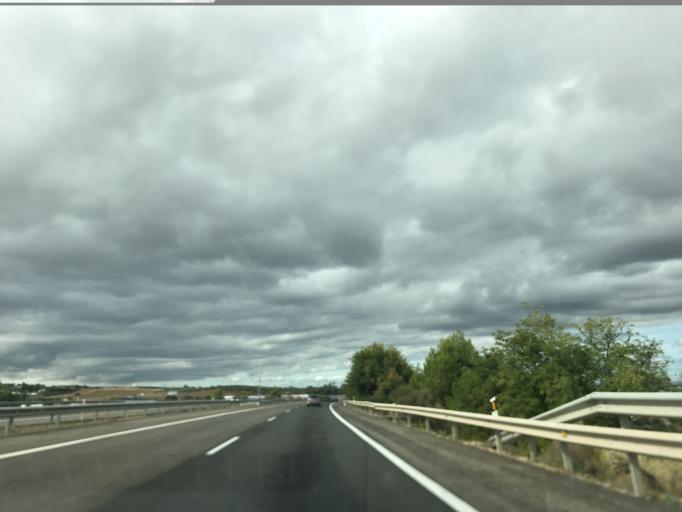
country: ES
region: Andalusia
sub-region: Province of Cordoba
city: Villa del Rio
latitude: 37.9863
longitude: -4.2980
